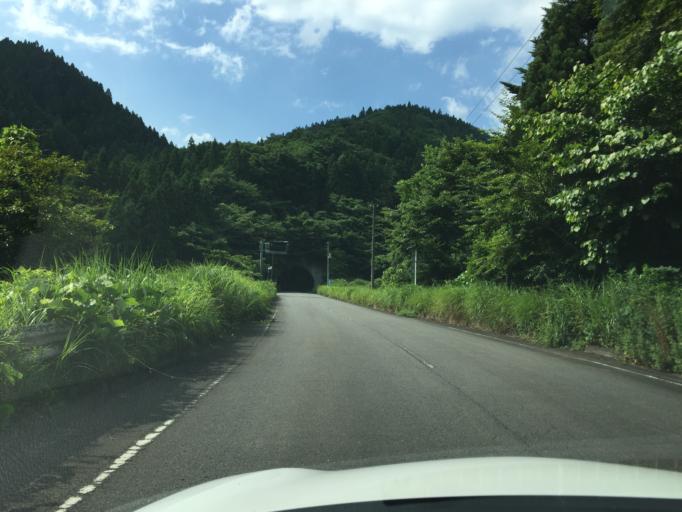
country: JP
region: Fukushima
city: Iwaki
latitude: 37.0844
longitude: 140.6826
